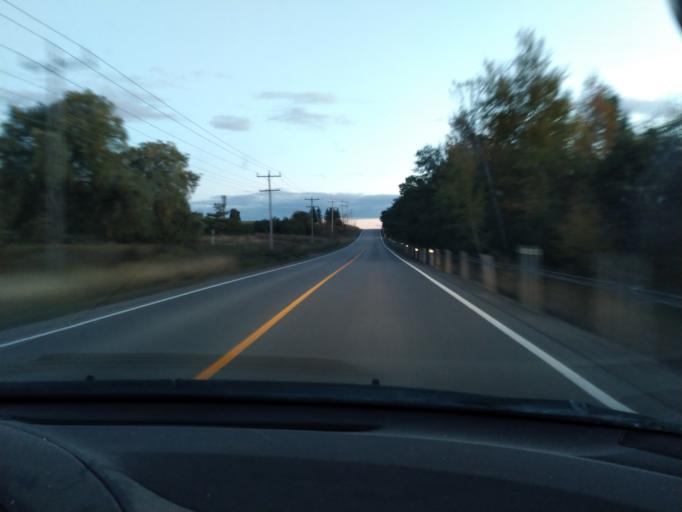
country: CA
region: Ontario
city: Innisfil
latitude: 44.2206
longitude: -79.6706
